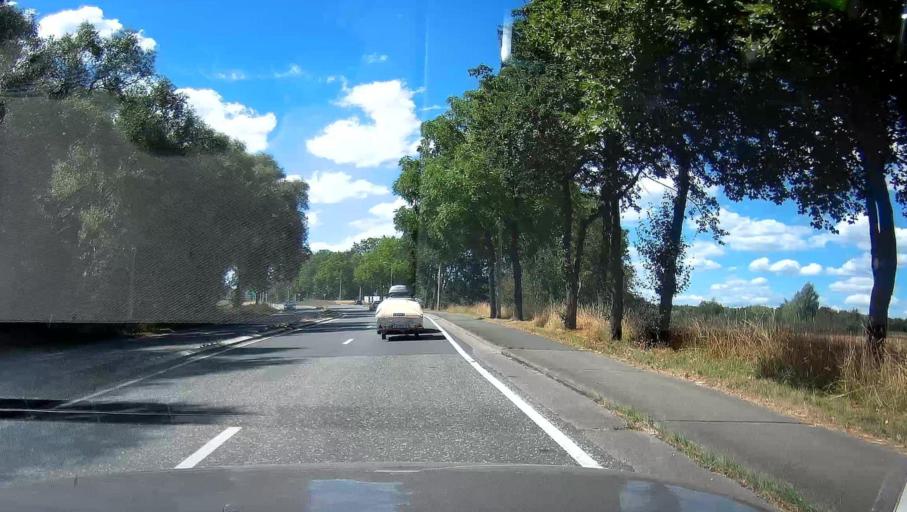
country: BE
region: Wallonia
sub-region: Province du Brabant Wallon
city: Genappe
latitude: 50.6142
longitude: 4.4561
